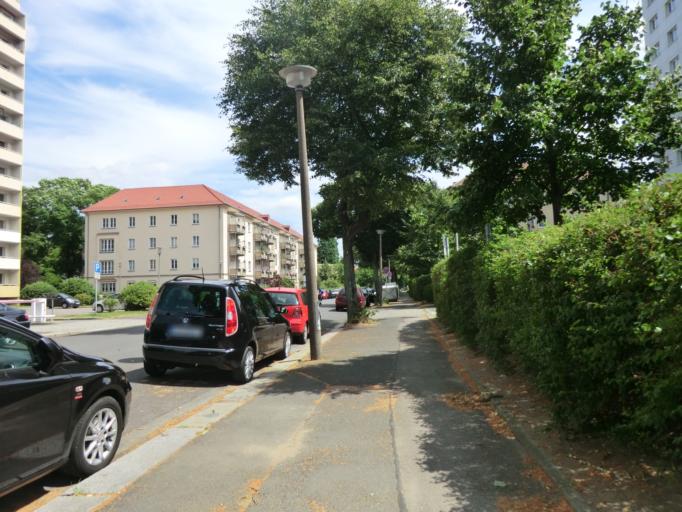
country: DE
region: Saxony
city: Dresden
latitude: 51.0385
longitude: 13.7185
